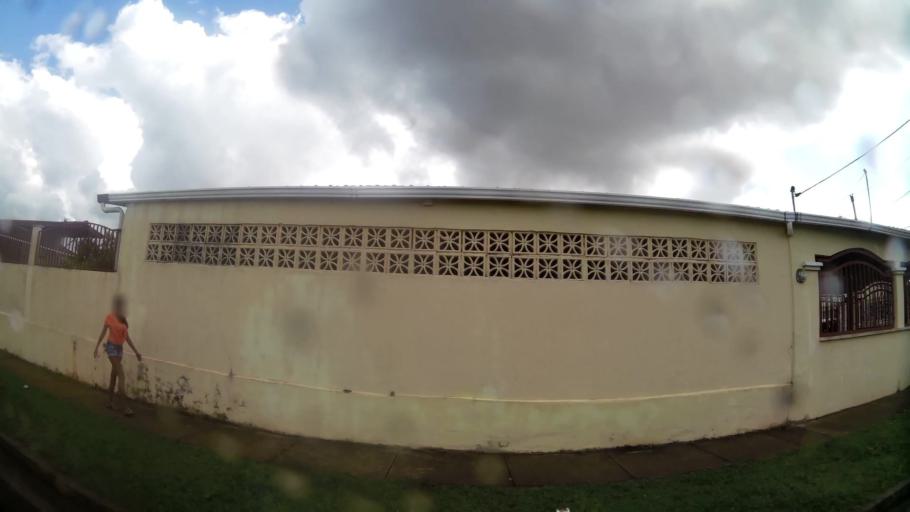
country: PA
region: Panama
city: Nuevo Arraijan
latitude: 8.9398
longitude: -79.7392
